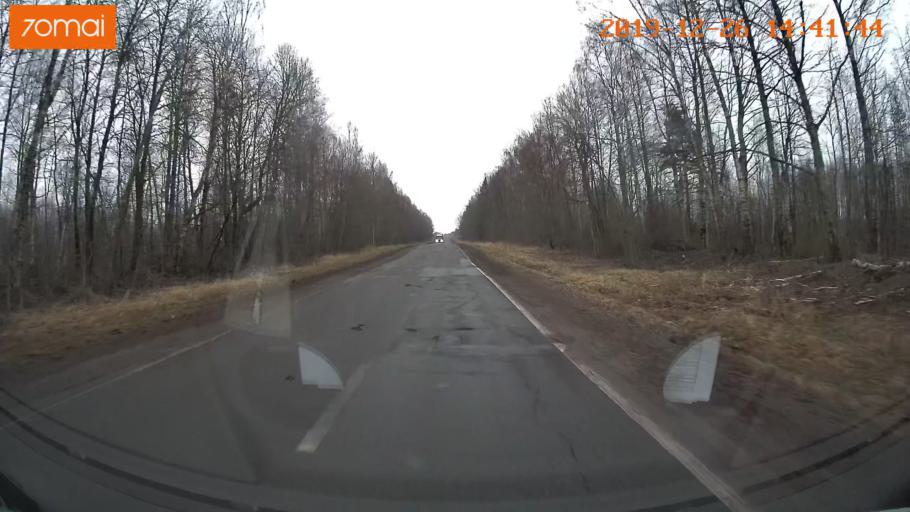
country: RU
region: Jaroslavl
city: Poshekhon'ye
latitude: 58.3688
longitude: 39.0230
